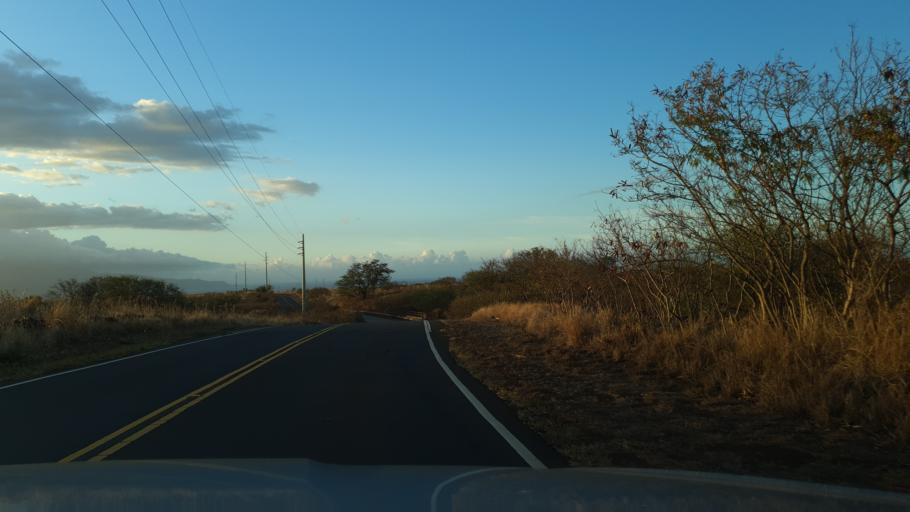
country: US
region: Hawaii
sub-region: Maui County
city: Pukalani
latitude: 20.8121
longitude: -156.3829
